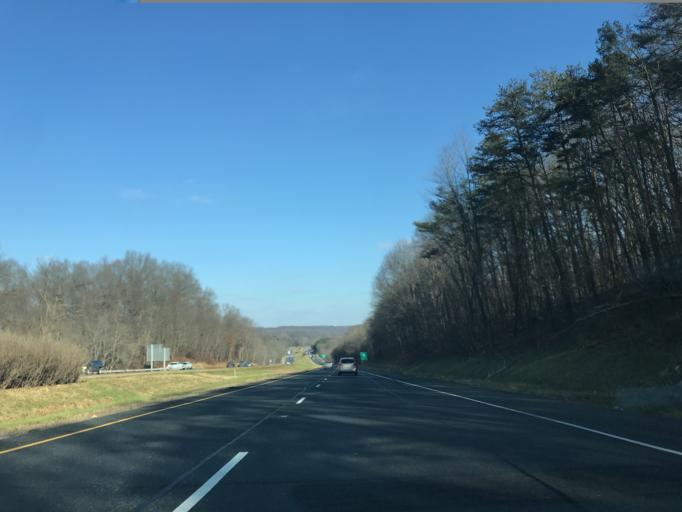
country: US
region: Pennsylvania
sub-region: York County
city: New Freedom
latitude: 39.6387
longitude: -76.6699
